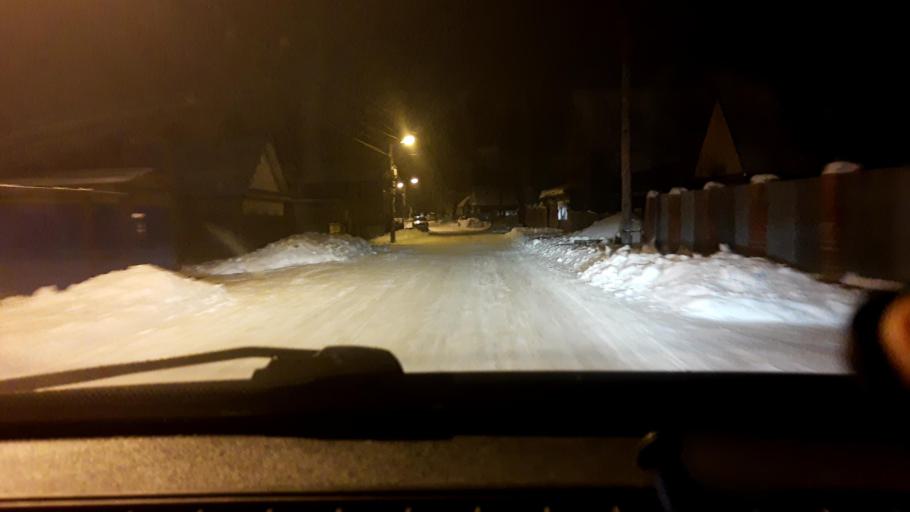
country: RU
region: Bashkortostan
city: Iglino
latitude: 54.8365
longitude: 56.1826
